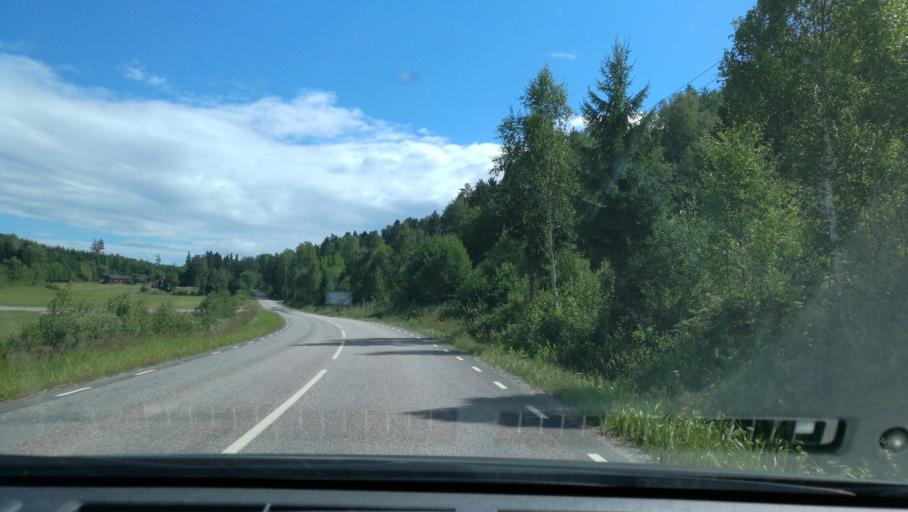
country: SE
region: OEstergoetland
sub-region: Norrkopings Kommun
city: Krokek
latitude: 58.6682
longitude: 16.4382
